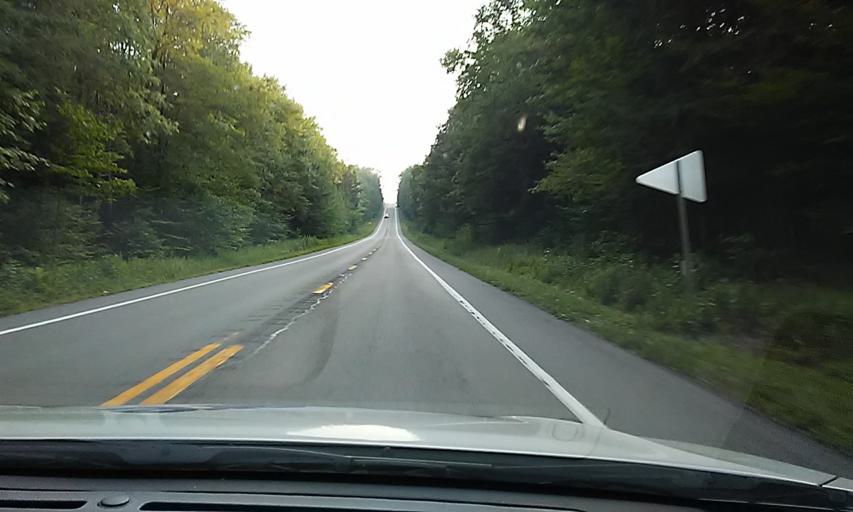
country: US
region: Pennsylvania
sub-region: Warren County
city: Sheffield
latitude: 41.5634
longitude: -78.9872
